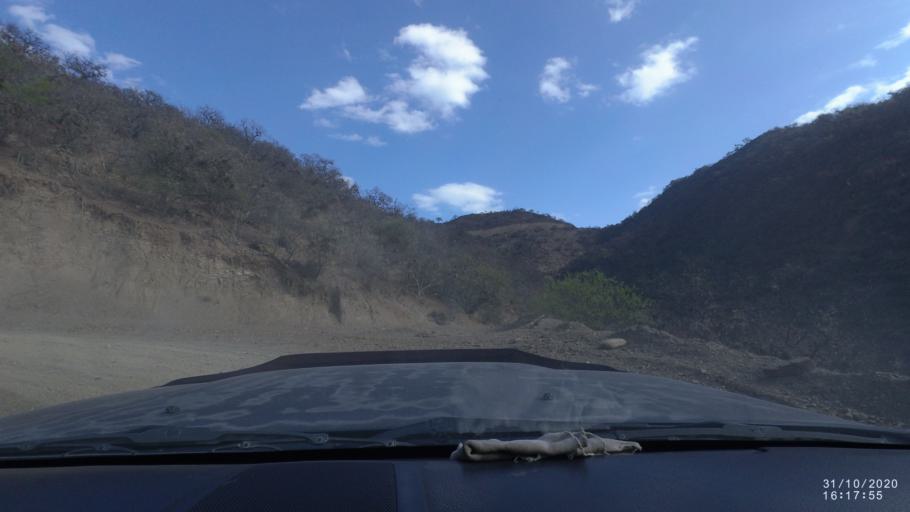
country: BO
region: Chuquisaca
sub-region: Provincia Zudanez
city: Mojocoya
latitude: -18.3927
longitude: -64.6045
